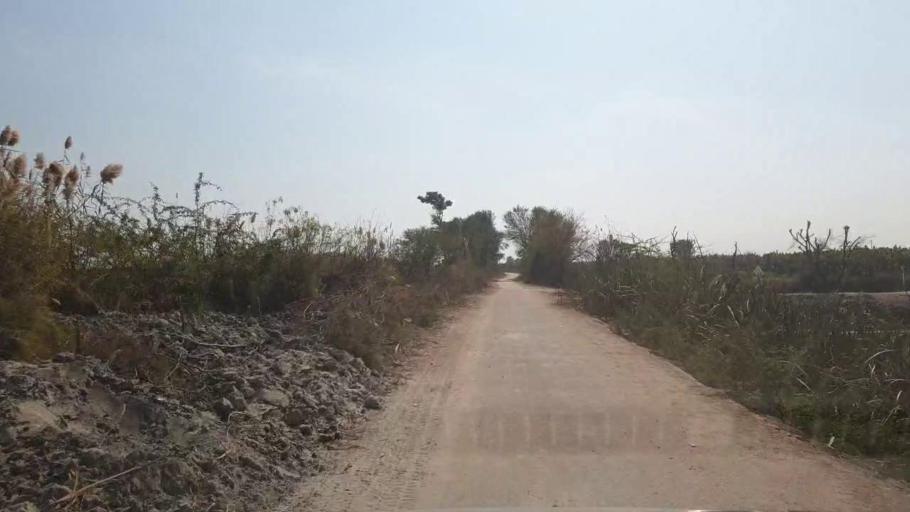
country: PK
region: Sindh
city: Chambar
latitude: 25.3565
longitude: 68.8219
